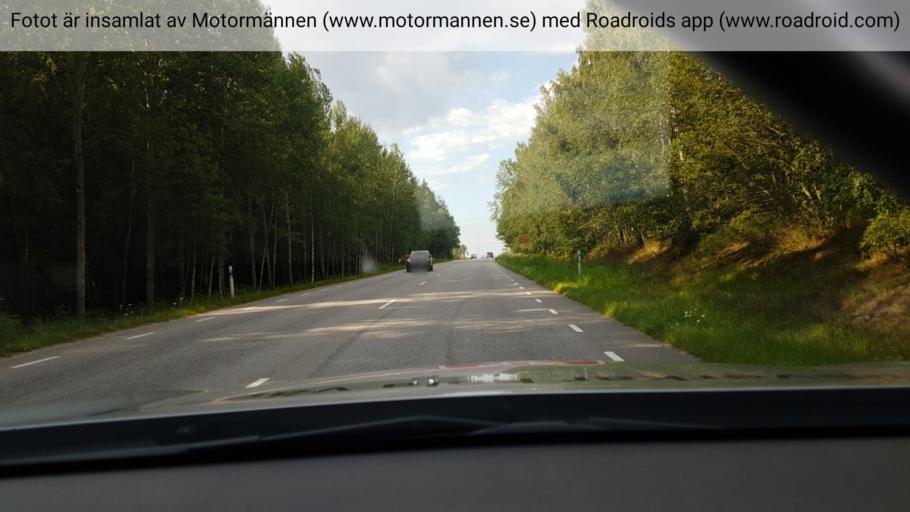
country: SE
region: Vaestra Goetaland
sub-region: Lidkopings Kommun
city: Lidkoping
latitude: 58.5282
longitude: 13.1115
